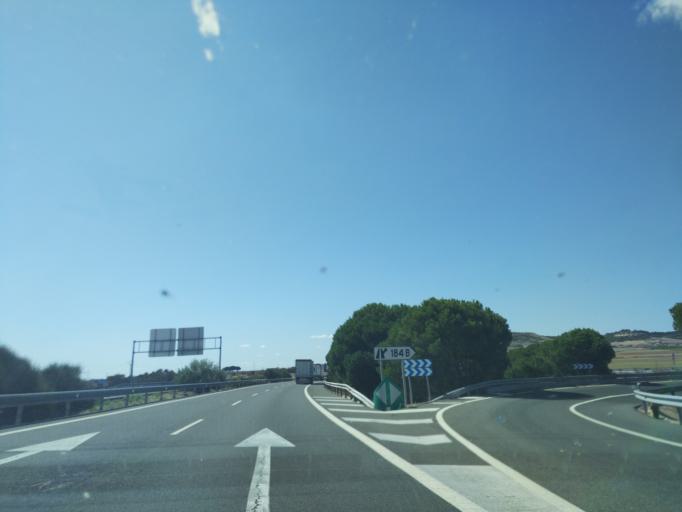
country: ES
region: Castille and Leon
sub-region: Provincia de Valladolid
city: Tordesillas
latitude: 41.5136
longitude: -5.0220
